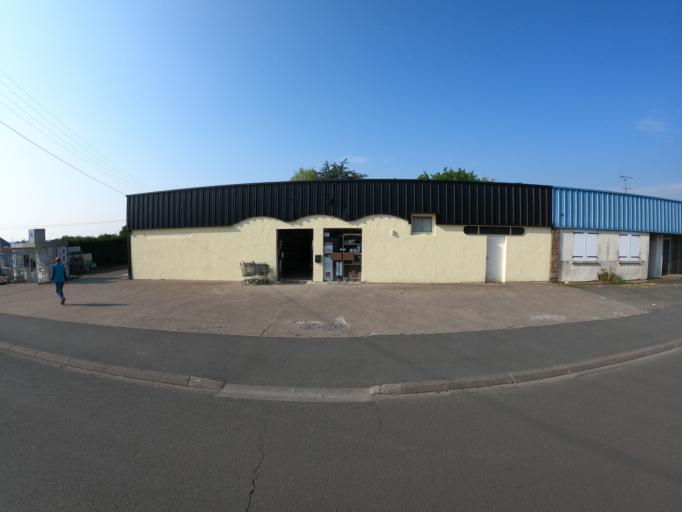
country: FR
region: Pays de la Loire
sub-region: Departement de Maine-et-Loire
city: La Seguiniere
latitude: 47.0635
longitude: -0.9423
